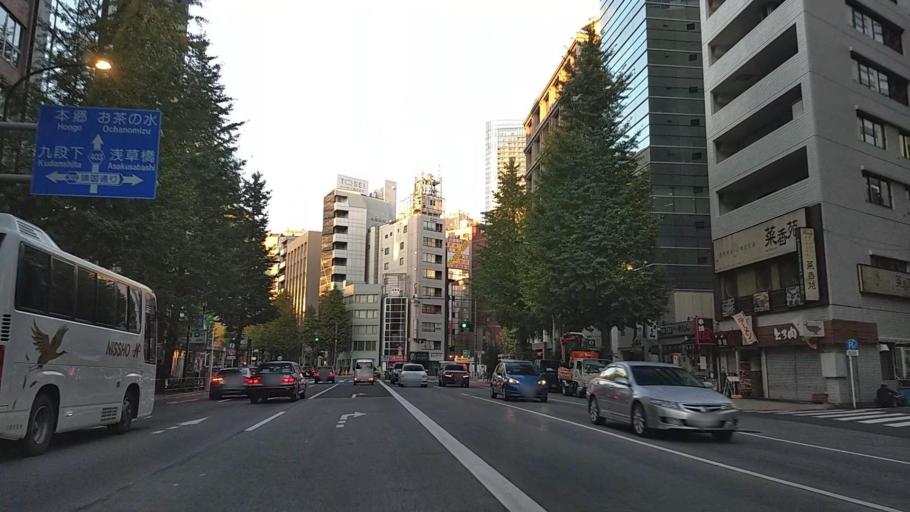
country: JP
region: Tokyo
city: Tokyo
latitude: 35.6937
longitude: 139.7653
